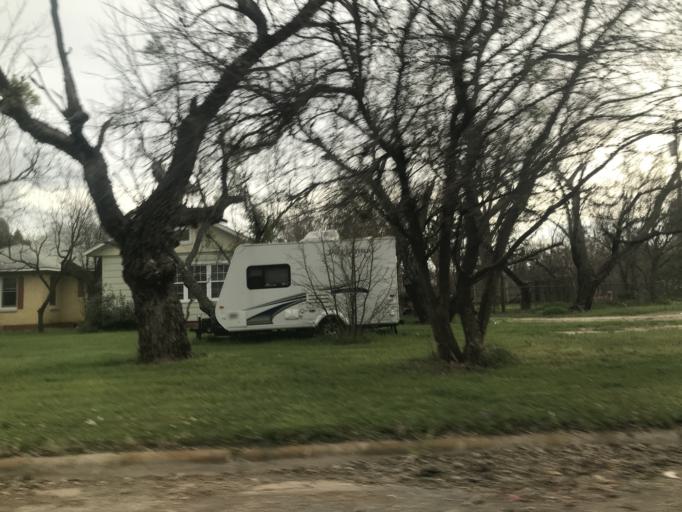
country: US
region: Texas
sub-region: Taylor County
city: Abilene
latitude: 32.4428
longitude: -99.7608
